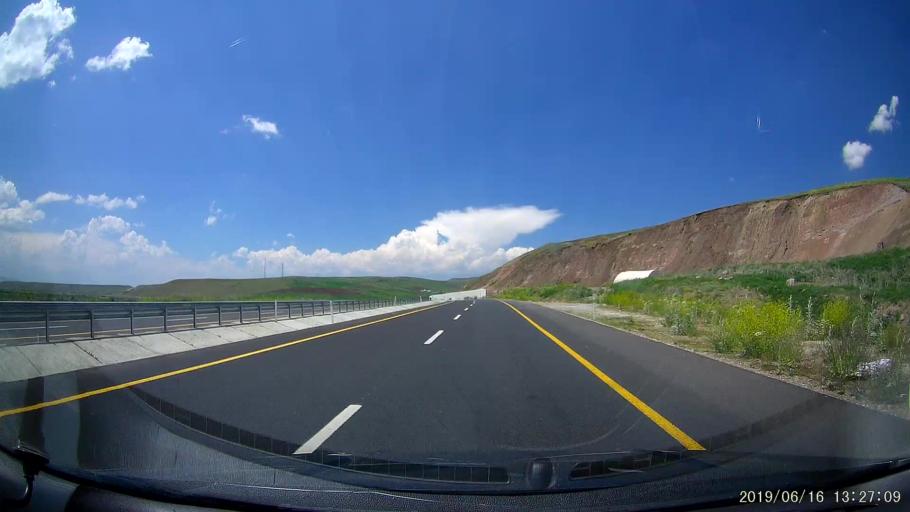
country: TR
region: Agri
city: Taslicay
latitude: 39.6675
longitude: 43.3153
